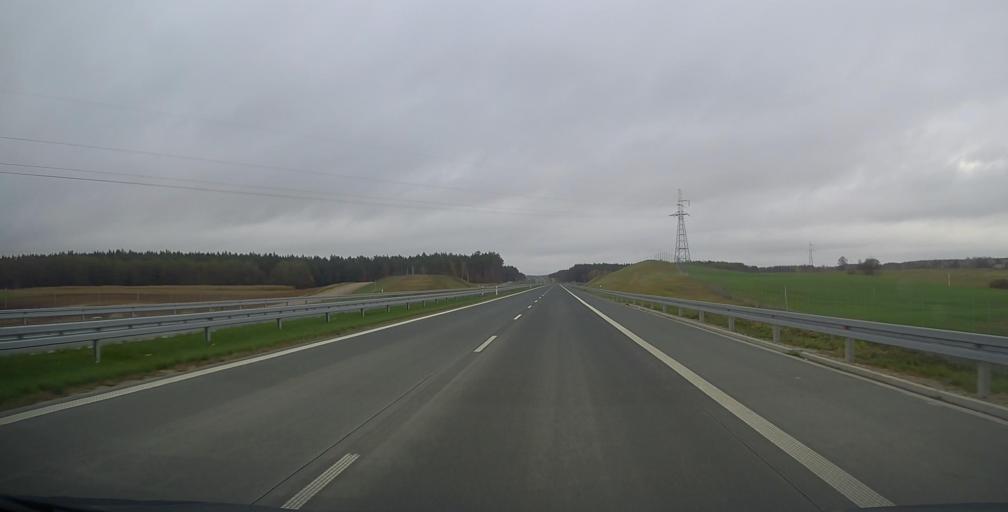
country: PL
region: Podlasie
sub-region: Powiat grajewski
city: Rajgrod
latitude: 53.8650
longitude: 22.6151
